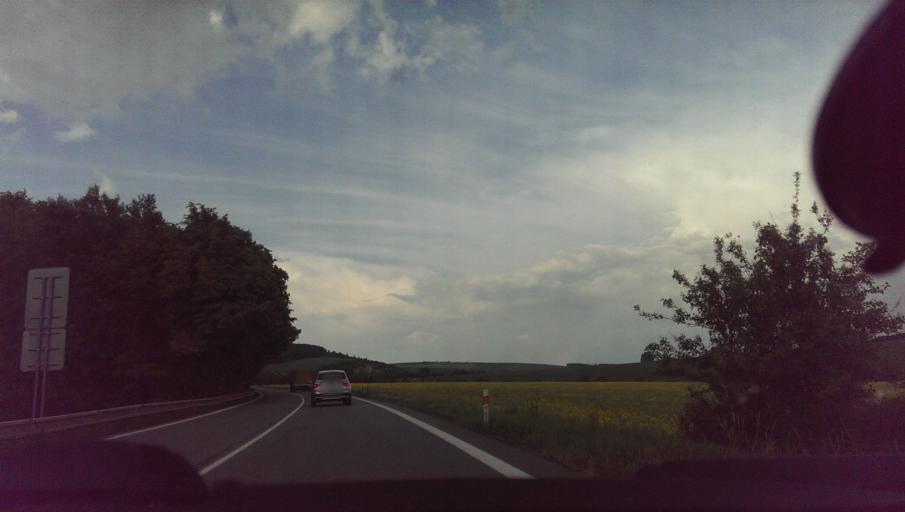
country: CZ
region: South Moravian
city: Nesovice
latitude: 49.1383
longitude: 17.0484
